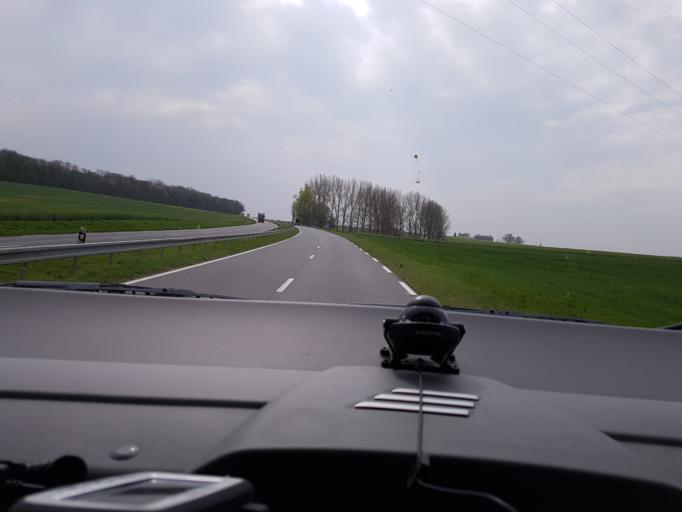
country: FR
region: Picardie
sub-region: Departement de l'Aisne
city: Jussy
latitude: 49.6851
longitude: 3.2565
